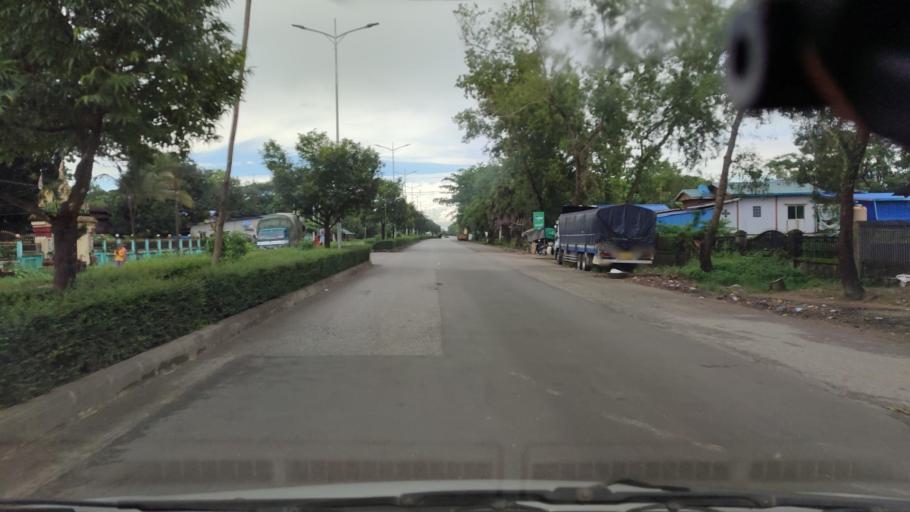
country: MM
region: Bago
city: Thanatpin
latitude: 17.1374
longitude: 96.2954
